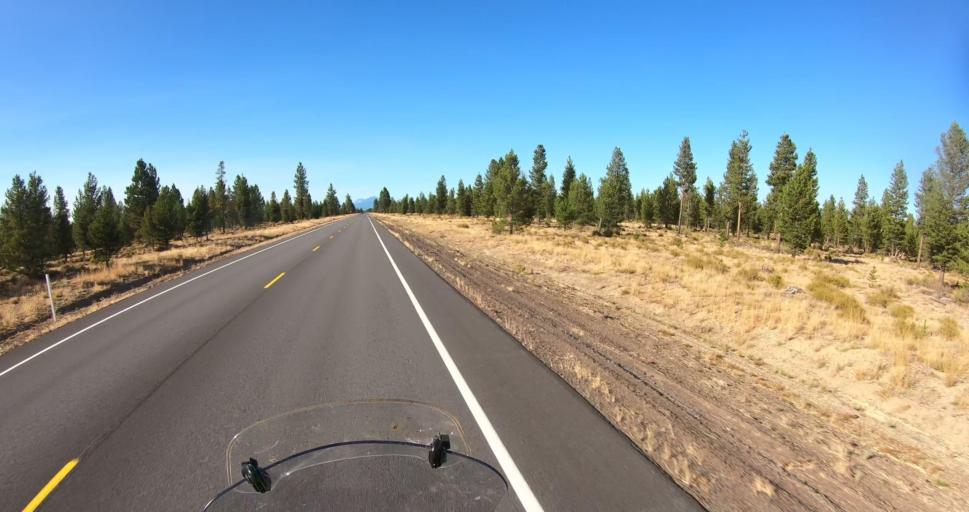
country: US
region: Oregon
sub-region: Deschutes County
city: La Pine
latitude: 43.6134
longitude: -121.5046
